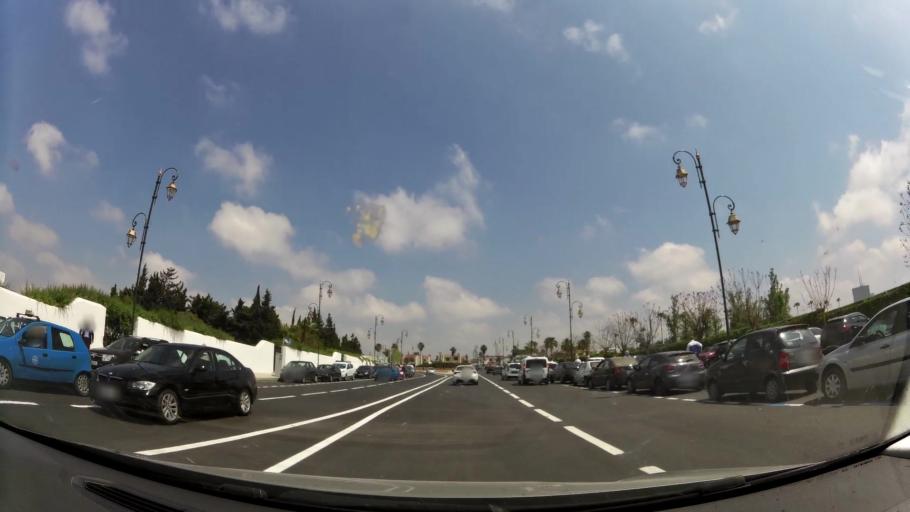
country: MA
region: Rabat-Sale-Zemmour-Zaer
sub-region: Skhirate-Temara
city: Temara
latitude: 33.9673
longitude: -6.8715
